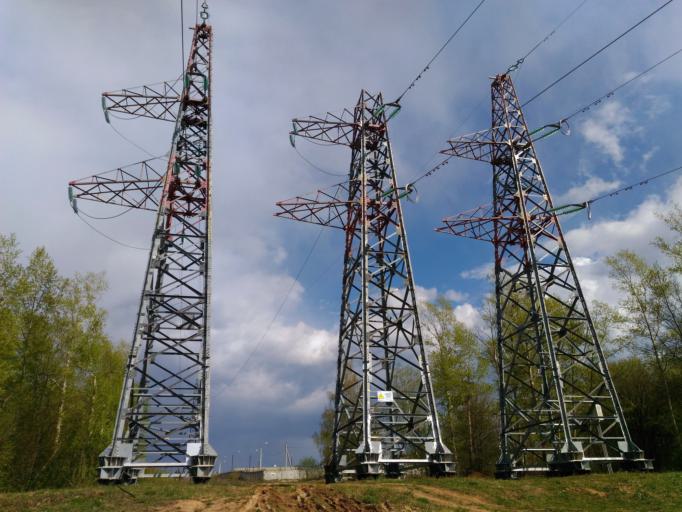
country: RU
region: Nizjnij Novgorod
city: Nizhniy Novgorod
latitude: 56.2913
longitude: 43.9725
